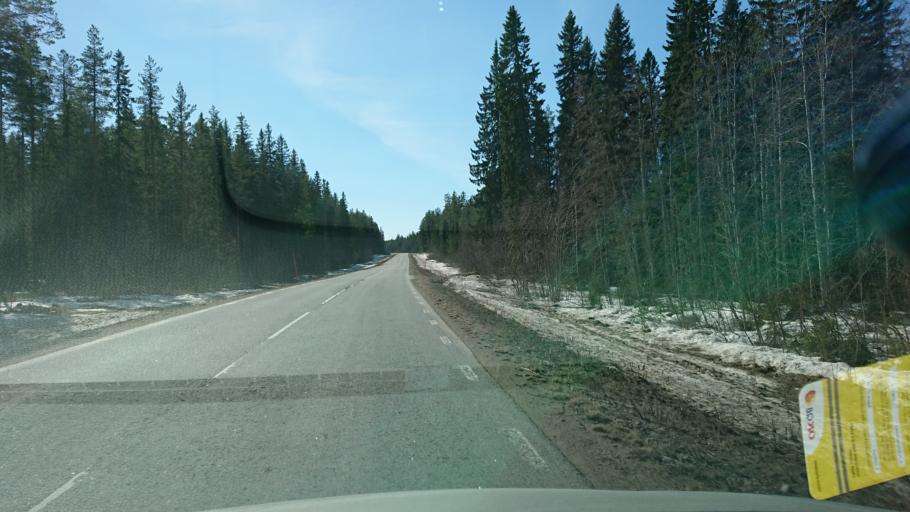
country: SE
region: Vaesternorrland
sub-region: Solleftea Kommun
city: As
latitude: 63.6267
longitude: 16.4389
